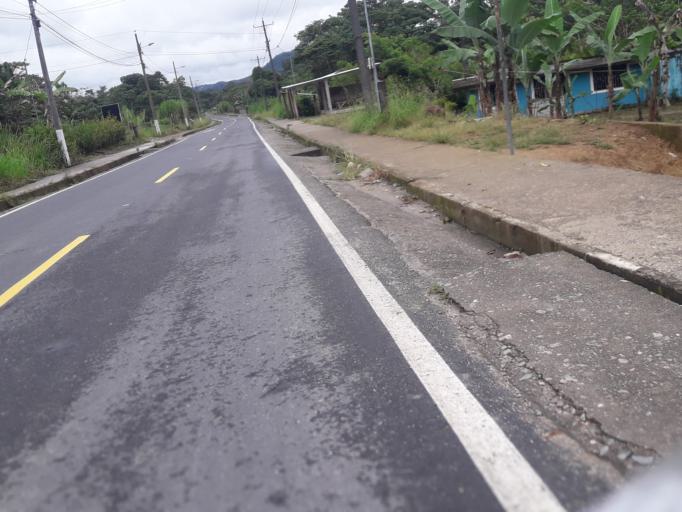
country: EC
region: Napo
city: Tena
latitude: -0.9597
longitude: -77.8594
